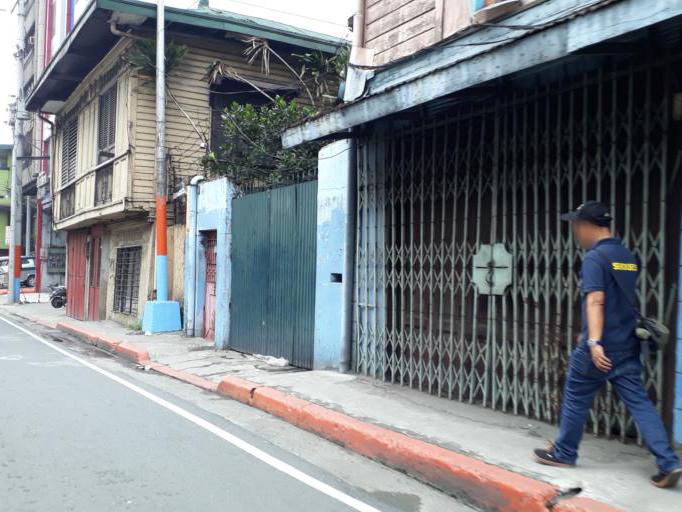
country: PH
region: Metro Manila
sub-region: City of Manila
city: Manila
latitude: 14.6088
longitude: 120.9757
